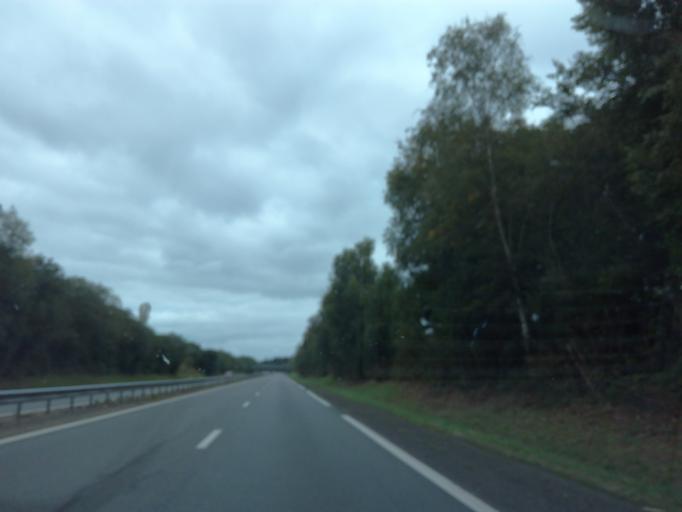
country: FR
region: Brittany
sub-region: Departement d'Ille-et-Vilaine
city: Saint-Meen-le-Grand
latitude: 48.1849
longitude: -2.2082
